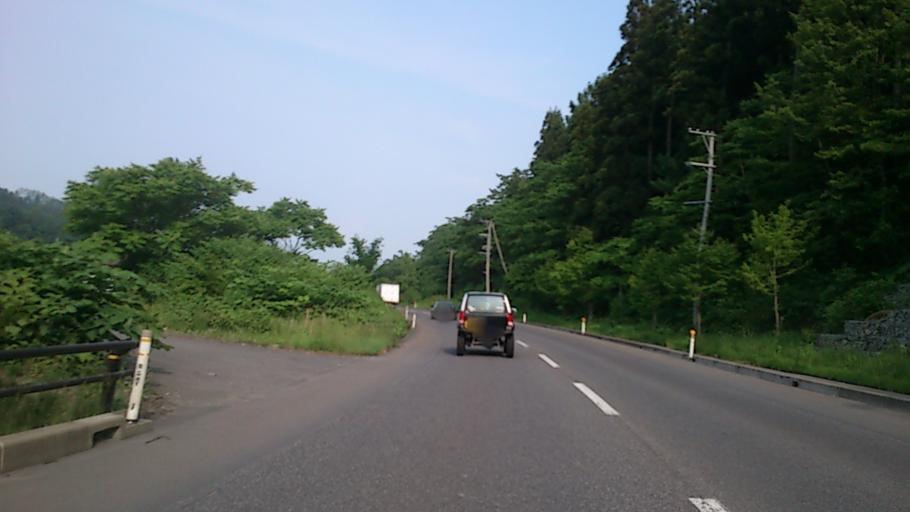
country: JP
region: Aomori
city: Hirosaki
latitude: 40.5895
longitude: 140.3752
